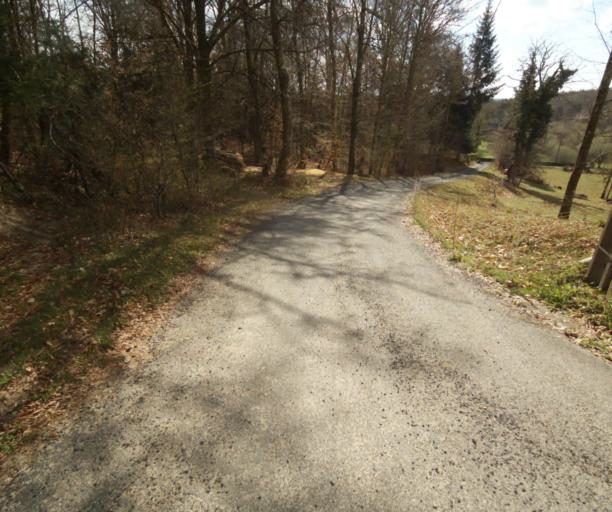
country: FR
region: Limousin
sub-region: Departement de la Correze
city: Argentat
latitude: 45.2396
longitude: 1.9524
